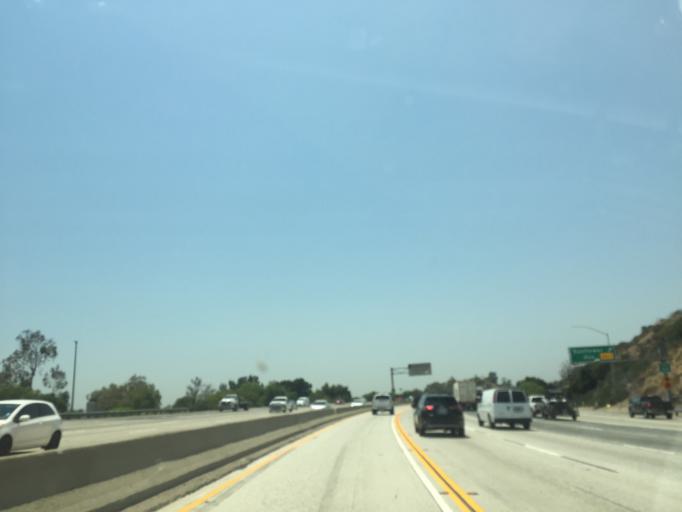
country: US
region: California
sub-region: Los Angeles County
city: Charter Oak
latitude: 34.1182
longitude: -117.8426
